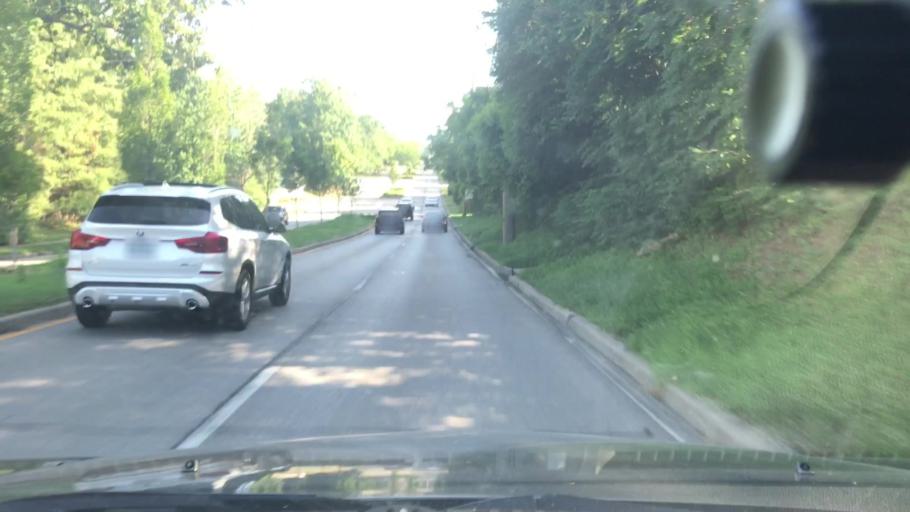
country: US
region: Missouri
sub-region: Saint Louis County
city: Creve Coeur
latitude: 38.6479
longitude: -90.4433
